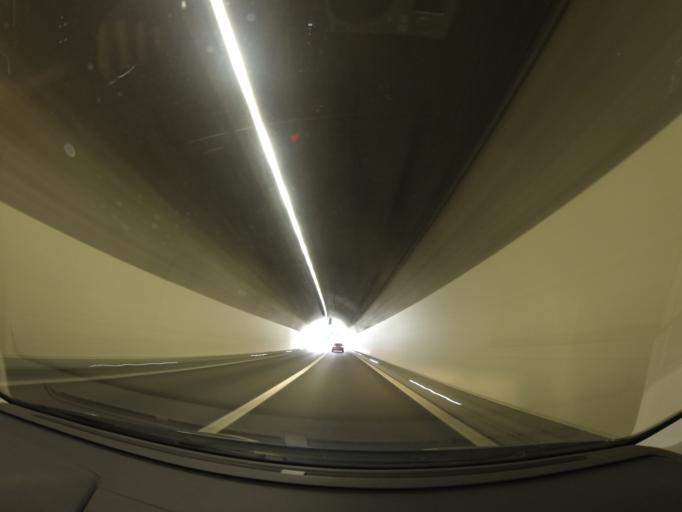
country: CH
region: Zurich
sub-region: Bezirk Hinwil
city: Rueti / Dorfzentrum, Suedl. Teil
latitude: 47.2349
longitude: 8.8650
